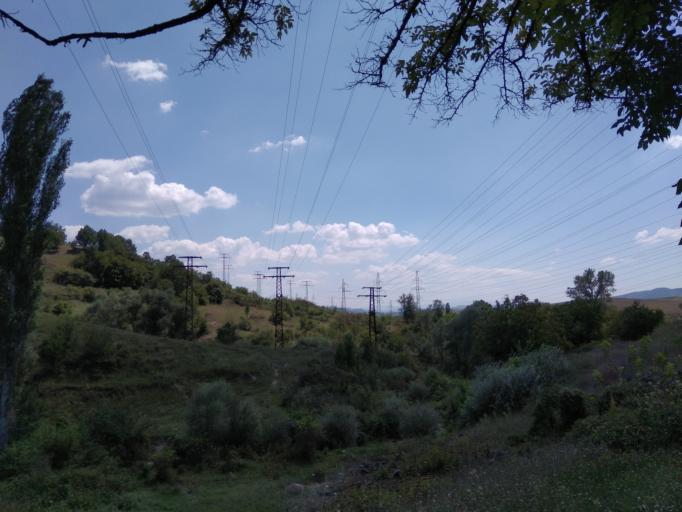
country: BG
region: Kurdzhali
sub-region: Obshtina Kurdzhali
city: Kurdzhali
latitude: 41.6545
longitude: 25.3989
